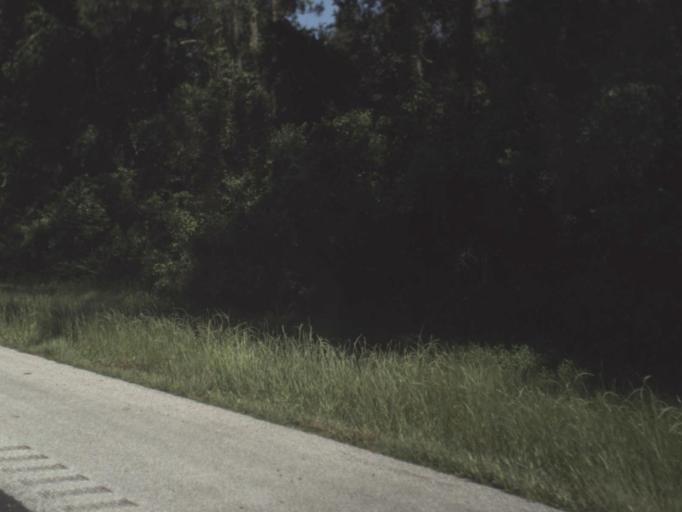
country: US
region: Florida
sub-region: Duval County
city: Baldwin
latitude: 30.2875
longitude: -82.0017
